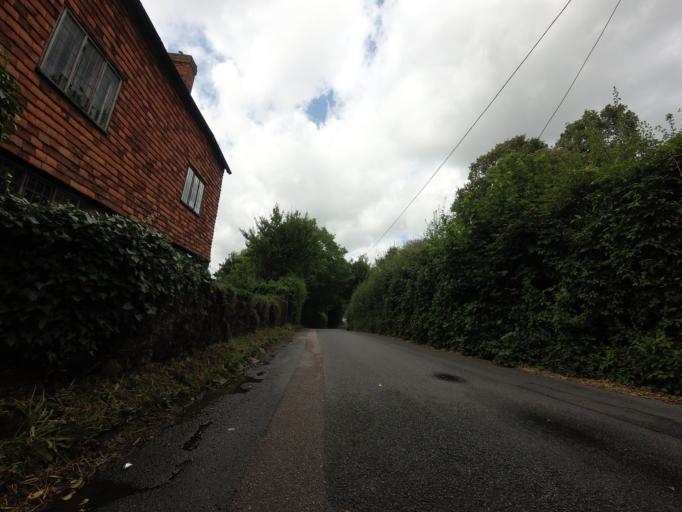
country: GB
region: England
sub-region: Kent
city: Hadlow
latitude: 51.2403
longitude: 0.3235
